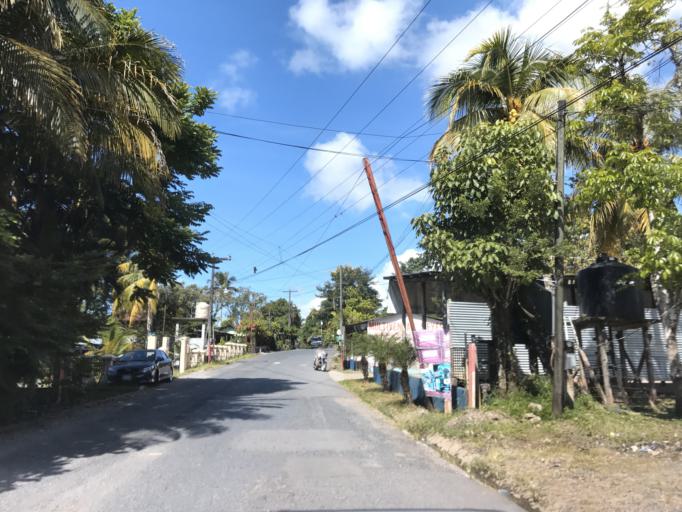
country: GT
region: Izabal
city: Morales
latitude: 15.6580
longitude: -89.0067
